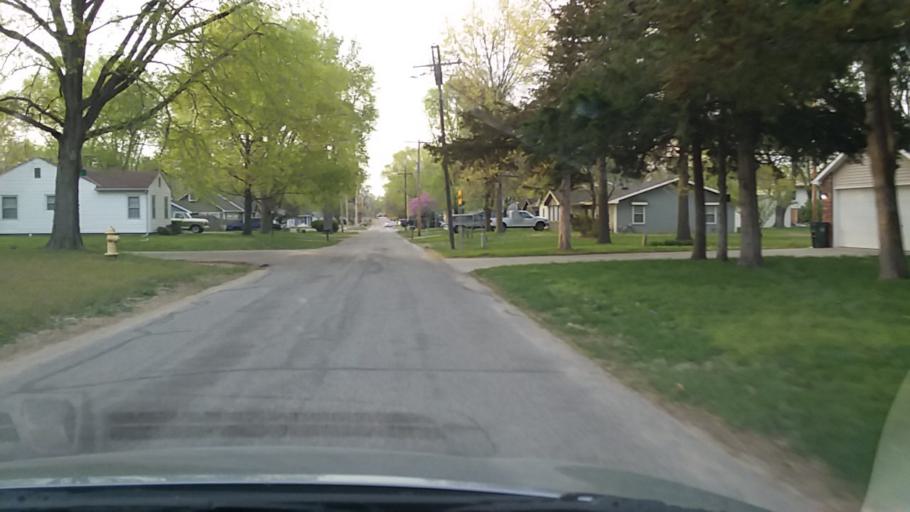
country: US
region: Kansas
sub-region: Douglas County
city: Lawrence
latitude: 38.9740
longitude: -95.2191
